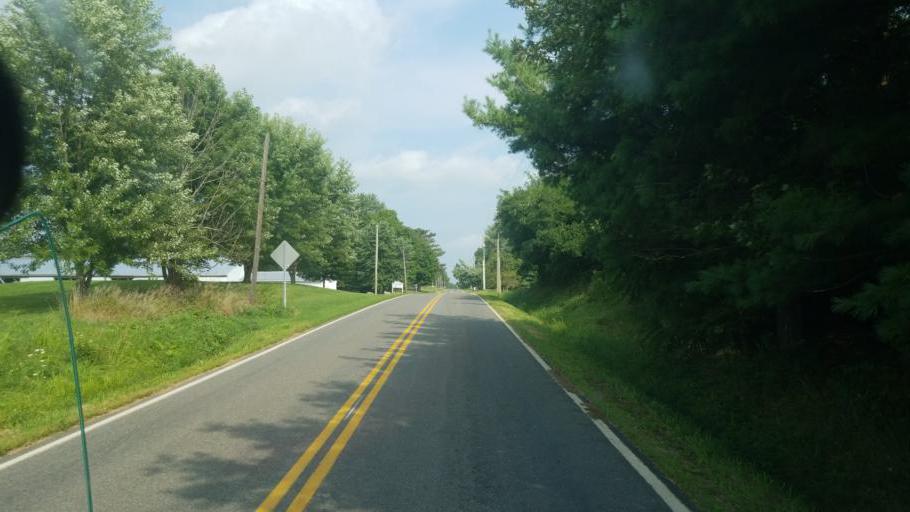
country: US
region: Ohio
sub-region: Medina County
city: Medina
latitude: 41.1423
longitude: -81.9212
